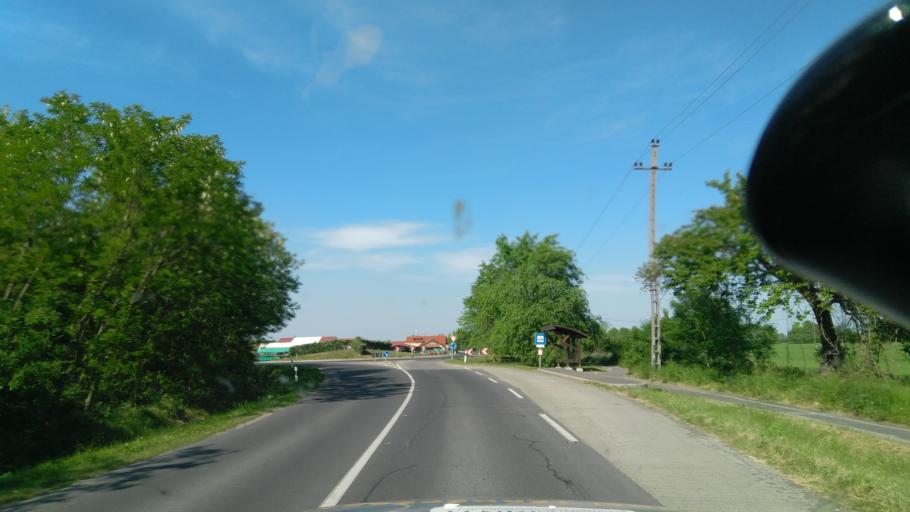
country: HU
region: Bekes
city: Sarkad
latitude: 46.7167
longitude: 21.3313
